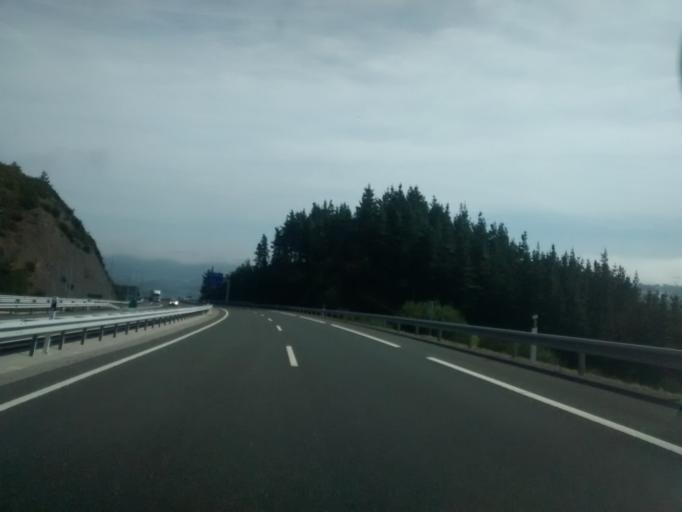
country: ES
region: Basque Country
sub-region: Provincia de Guipuzcoa
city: Eskoriatza
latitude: 43.0170
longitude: -2.5333
